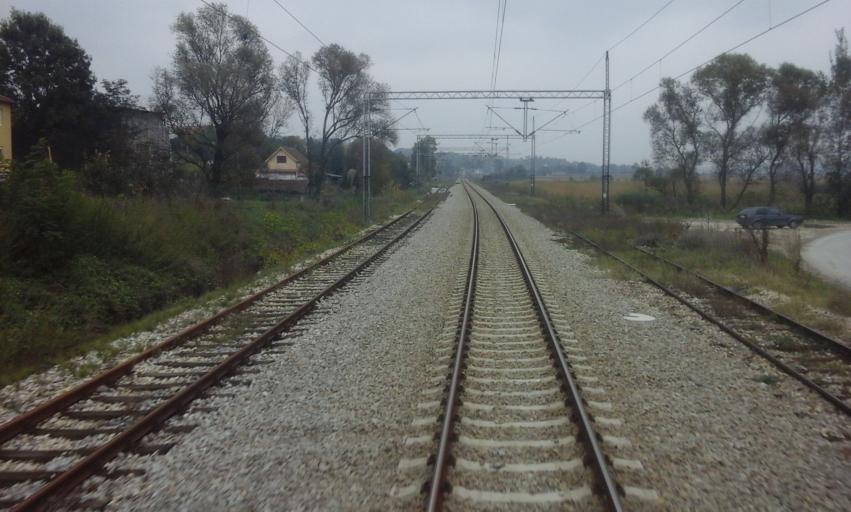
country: RS
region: Central Serbia
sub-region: Belgrade
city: Mladenovac
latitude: 44.4832
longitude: 20.6583
